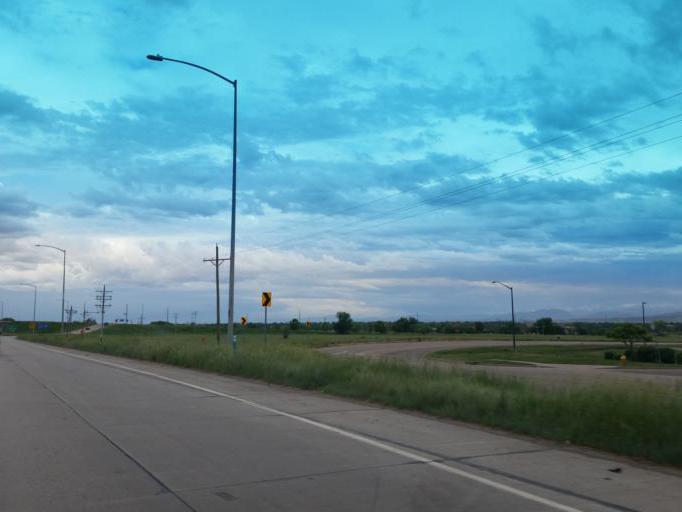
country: US
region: Colorado
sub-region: Larimer County
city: Fort Collins
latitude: 40.5709
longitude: -105.0015
